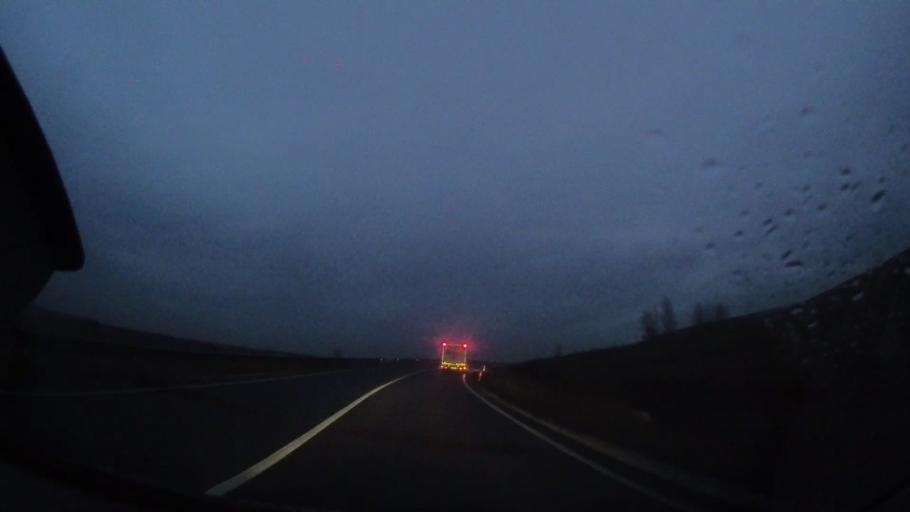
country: RO
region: Harghita
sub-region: Comuna Subcetate
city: Subcetate
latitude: 46.8476
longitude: 25.4689
